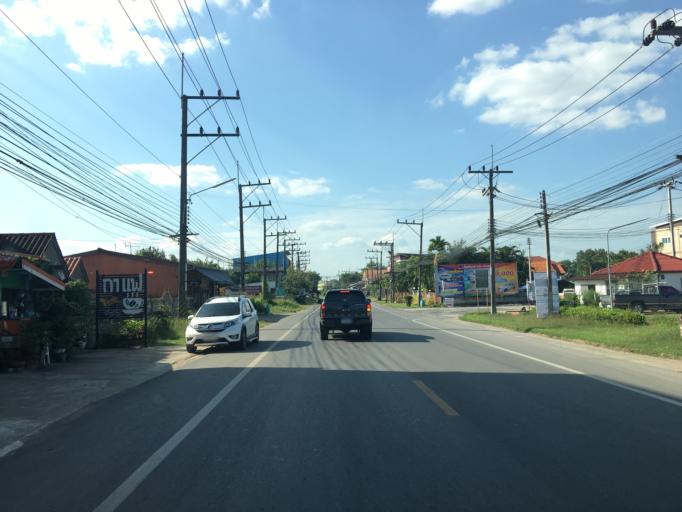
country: TH
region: Phayao
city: Chun
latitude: 19.3426
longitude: 100.1214
